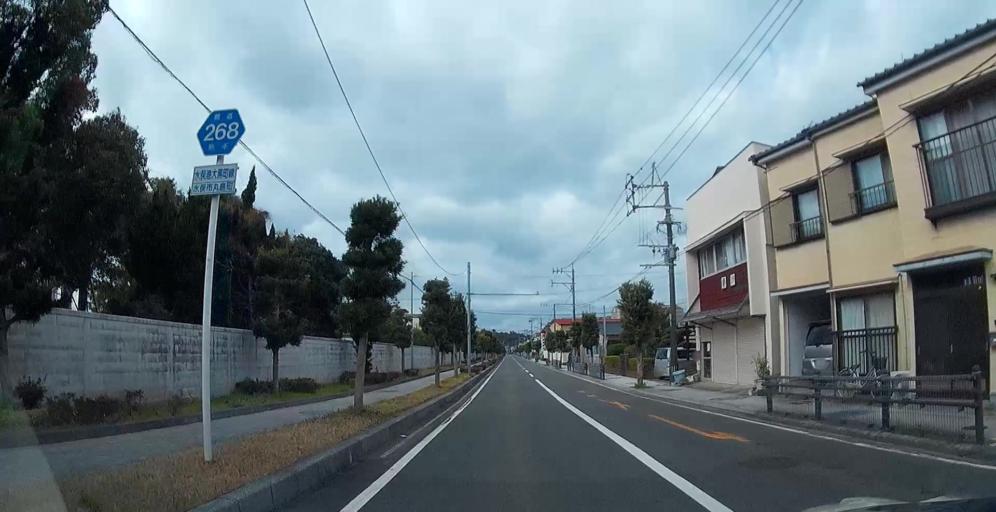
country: JP
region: Kumamoto
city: Minamata
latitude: 32.2105
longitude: 130.3958
